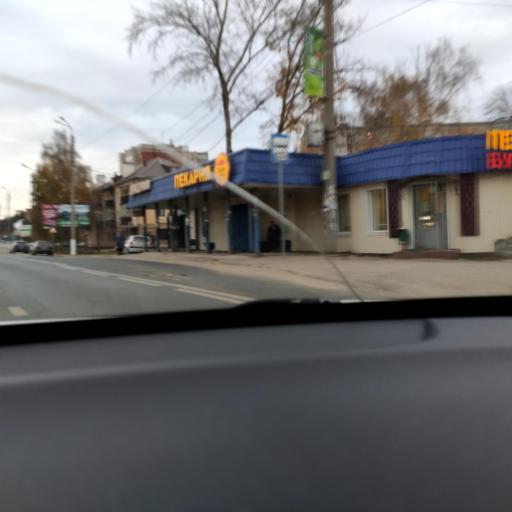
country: RU
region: Tatarstan
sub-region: Zelenodol'skiy Rayon
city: Zelenodolsk
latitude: 55.8487
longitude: 48.5611
